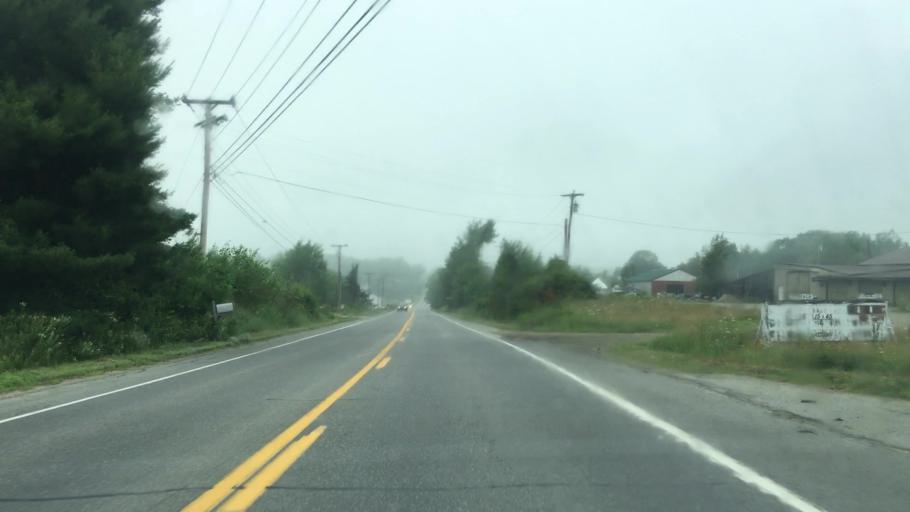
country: US
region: Maine
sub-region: Lincoln County
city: Wiscasset
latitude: 44.0387
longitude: -69.6734
